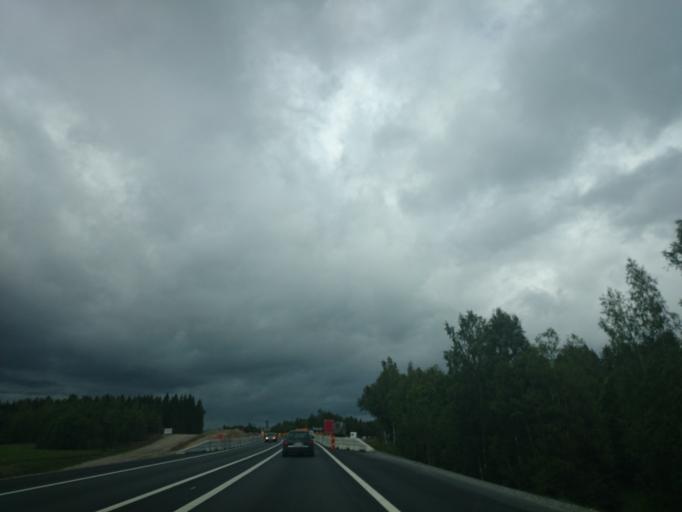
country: SE
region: Vaesternorrland
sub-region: Sundsvalls Kommun
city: Njurundabommen
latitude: 62.2517
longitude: 17.3715
